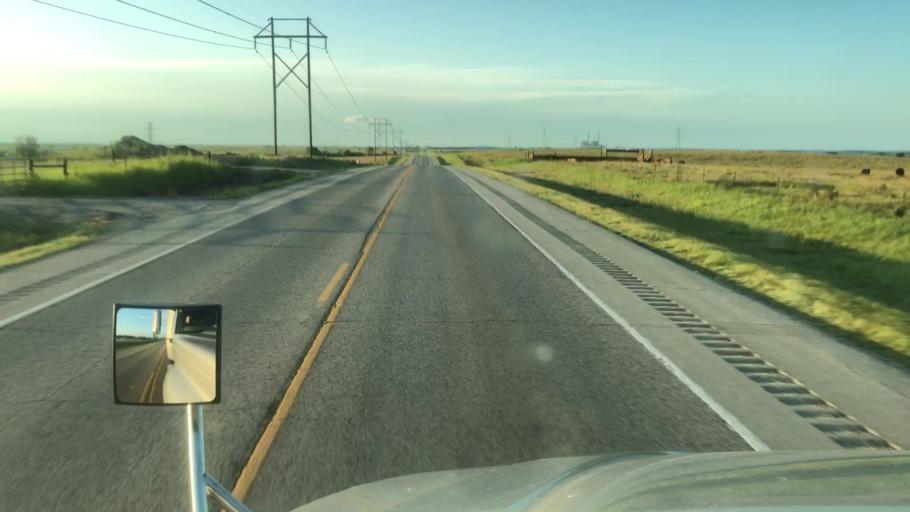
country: US
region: Oklahoma
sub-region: Noble County
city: Perry
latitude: 36.3923
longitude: -97.0676
